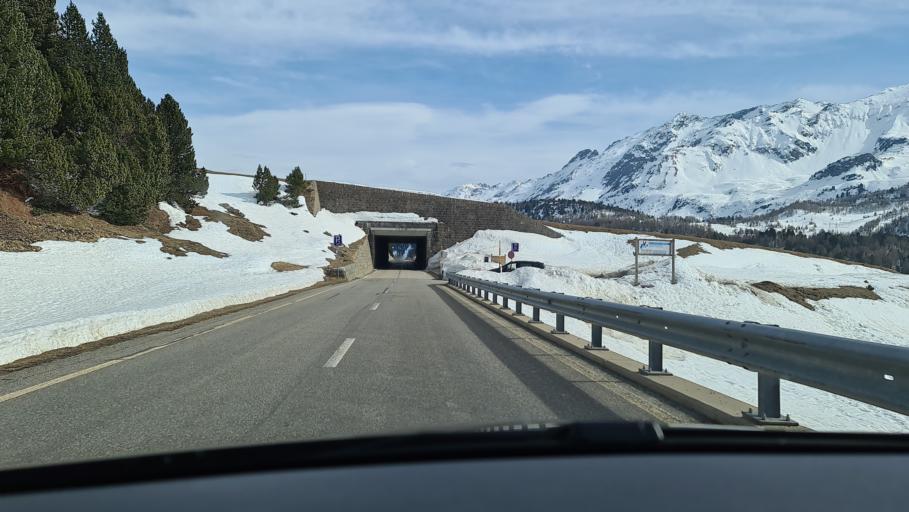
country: CH
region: Ticino
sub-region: Leventina District
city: Faido
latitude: 46.5514
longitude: 8.8097
